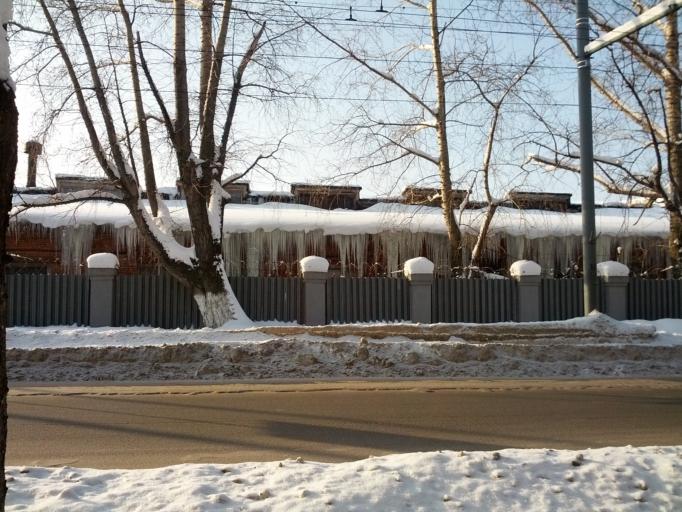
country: RU
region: Mariy-El
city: Yoshkar-Ola
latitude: 56.6378
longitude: 47.8629
